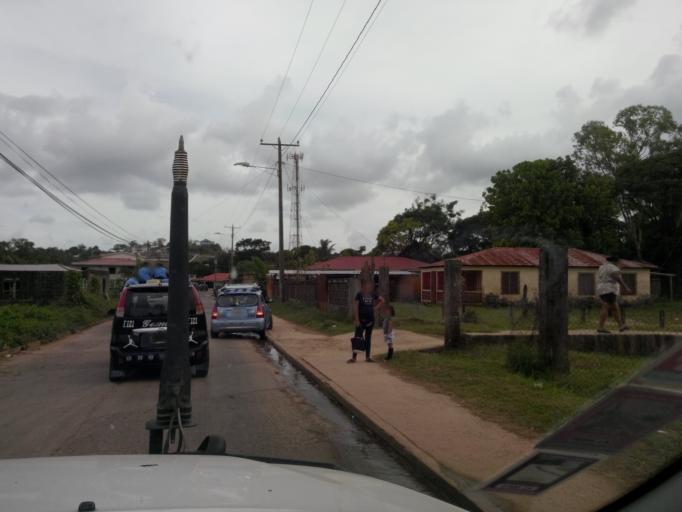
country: NI
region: Atlantico Sur
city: Bluefields
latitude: 12.0277
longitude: -83.7679
